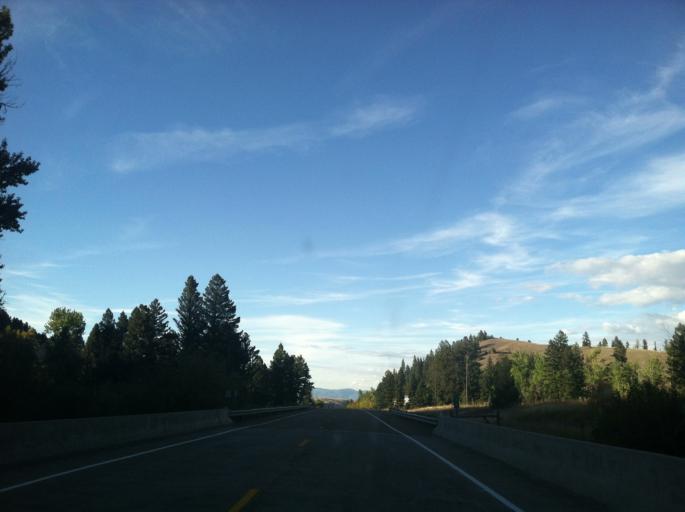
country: US
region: Montana
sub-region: Granite County
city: Philipsburg
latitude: 46.4705
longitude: -113.2347
